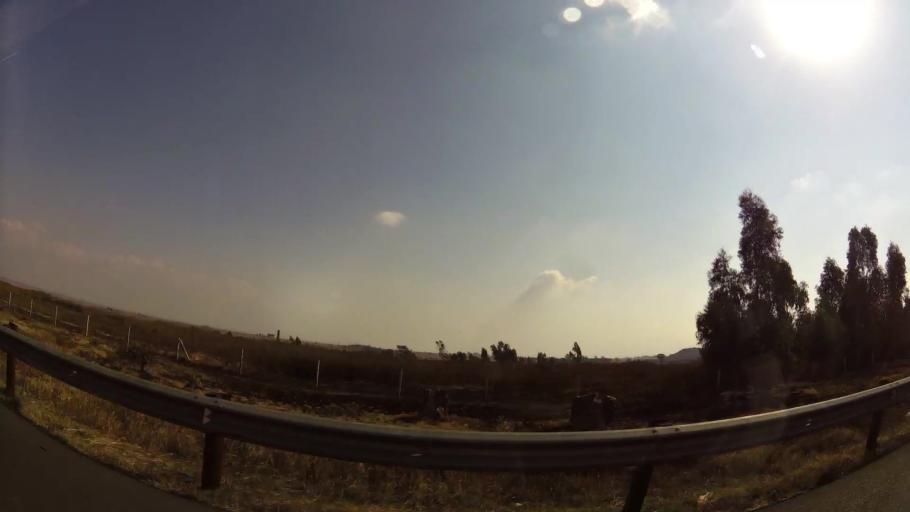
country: ZA
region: Gauteng
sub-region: Ekurhuleni Metropolitan Municipality
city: Springs
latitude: -26.1574
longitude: 28.5216
